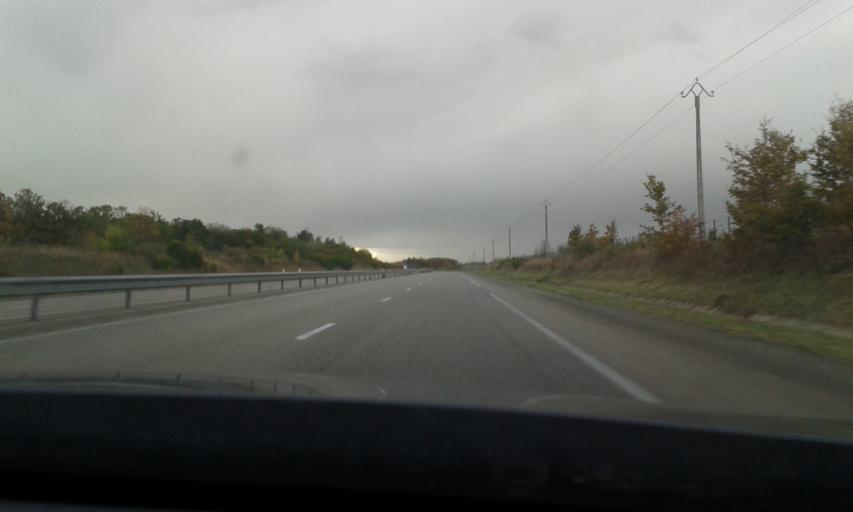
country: FR
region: Haute-Normandie
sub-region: Departement de l'Eure
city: Evreux
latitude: 48.9121
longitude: 1.1855
